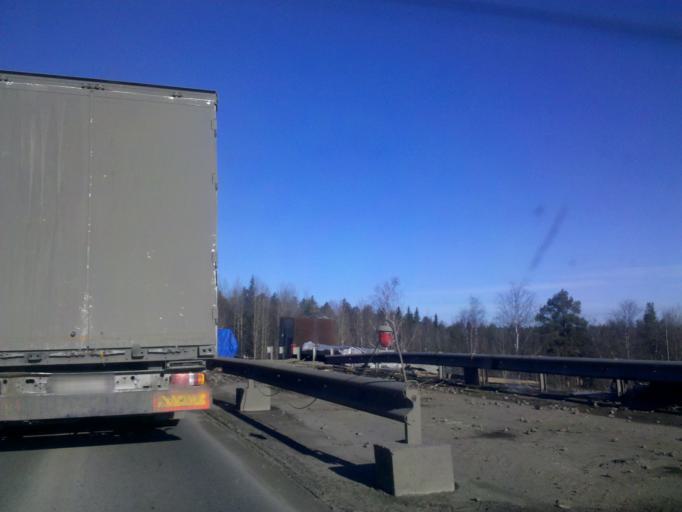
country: RU
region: Republic of Karelia
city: Kondopoga
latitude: 62.1848
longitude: 34.2113
